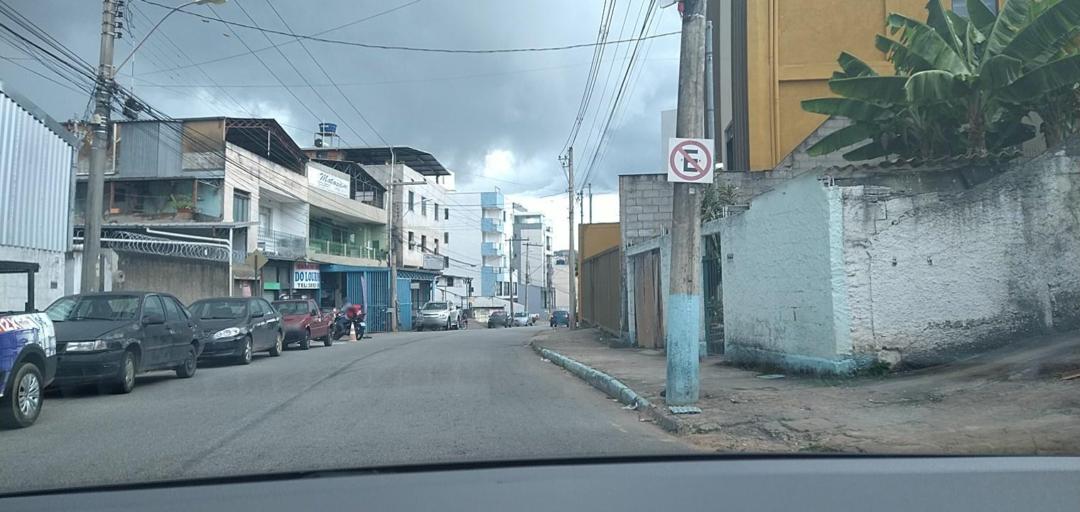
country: BR
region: Minas Gerais
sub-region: Joao Monlevade
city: Joao Monlevade
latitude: -19.8083
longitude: -43.1832
